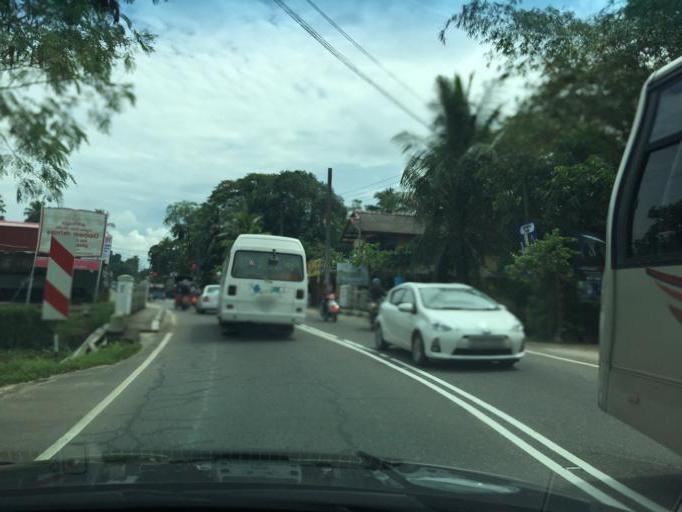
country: LK
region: Western
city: Horana South
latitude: 6.7215
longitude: 80.0428
